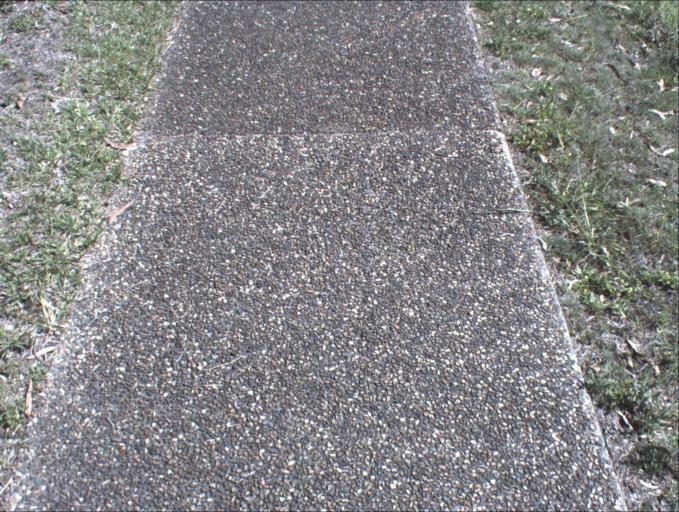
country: AU
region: Queensland
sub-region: Logan
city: Beenleigh
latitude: -27.7008
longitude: 153.1722
